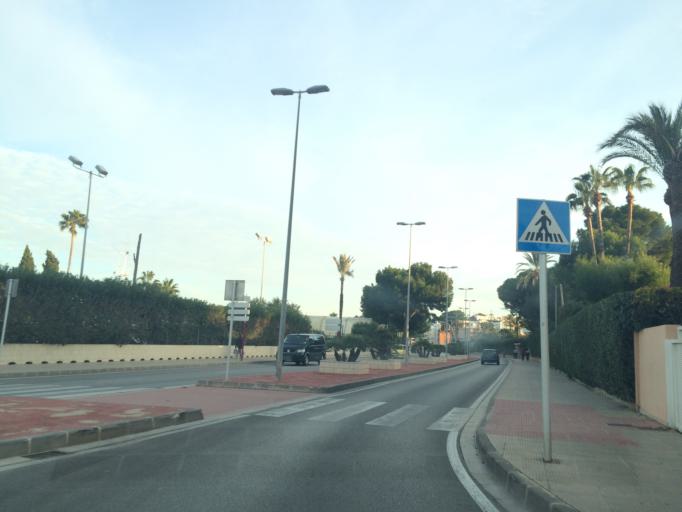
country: ES
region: Valencia
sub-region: Provincia de Alicante
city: Denia
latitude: 38.8386
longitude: 0.1149
